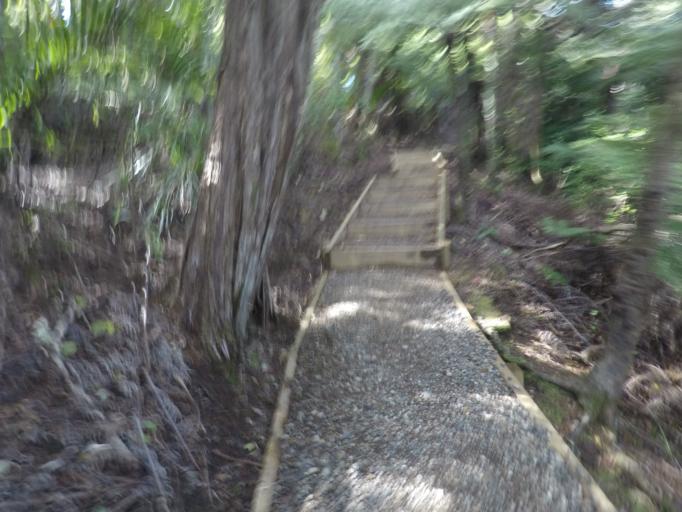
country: NZ
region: Auckland
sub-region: Auckland
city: Titirangi
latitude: -37.0326
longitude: 174.5215
